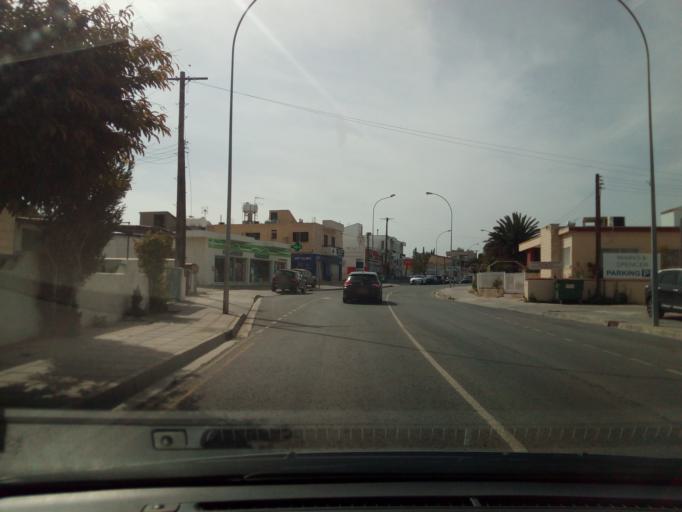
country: CY
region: Lefkosia
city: Kato Deftera
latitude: 35.1045
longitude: 33.3029
